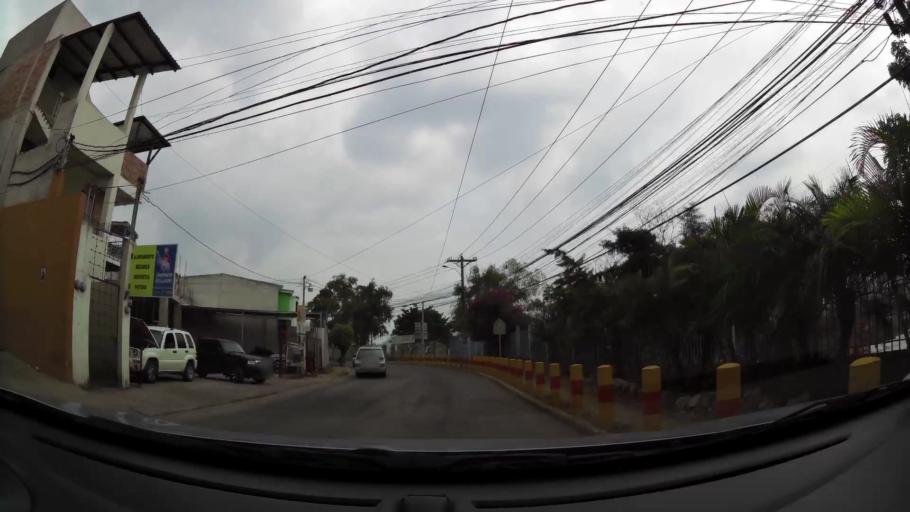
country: HN
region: Francisco Morazan
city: Tegucigalpa
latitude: 14.0930
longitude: -87.1658
